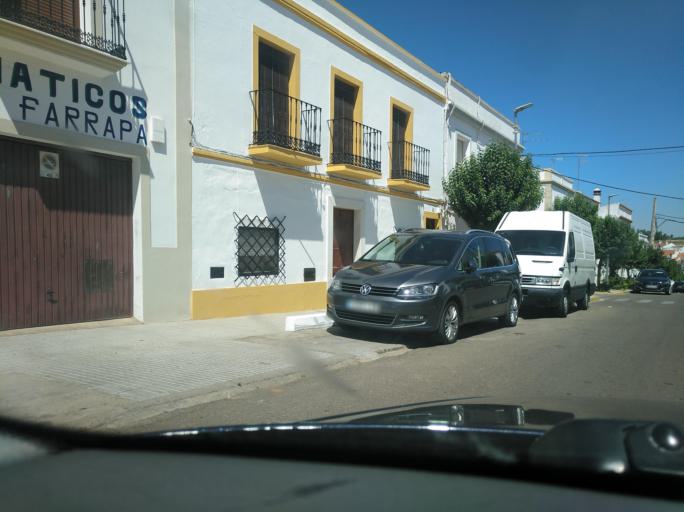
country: ES
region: Extremadura
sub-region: Provincia de Badajoz
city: Olivenza
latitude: 38.6795
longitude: -7.1025
